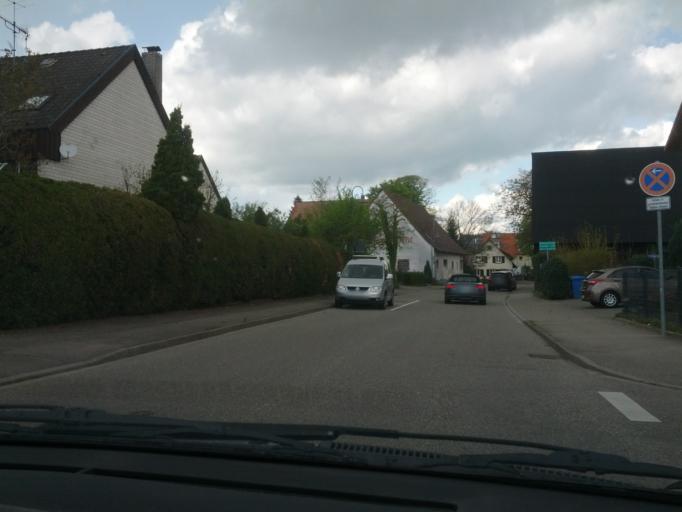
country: DE
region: Baden-Wuerttemberg
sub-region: Freiburg Region
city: Denzlingen
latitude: 48.0693
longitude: 7.8706
